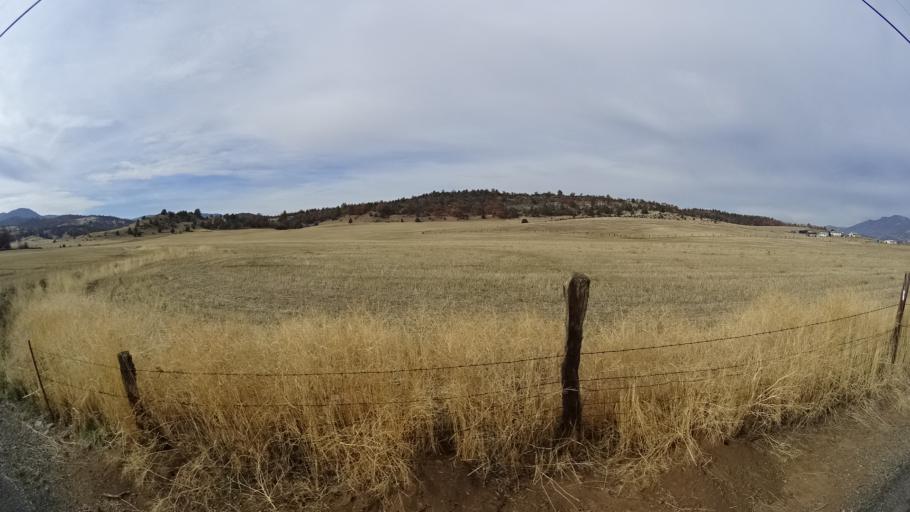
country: US
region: California
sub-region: Siskiyou County
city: Montague
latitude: 41.6975
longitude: -122.5640
